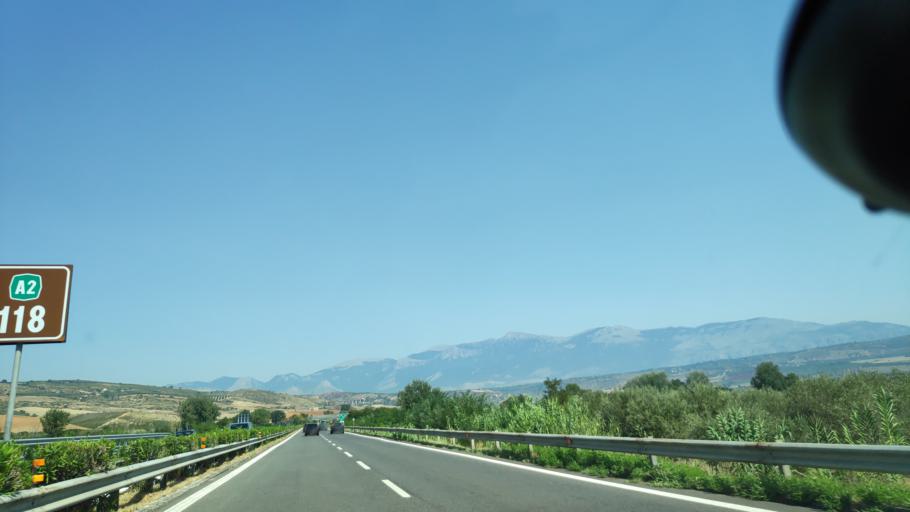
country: IT
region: Calabria
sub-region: Provincia di Cosenza
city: Firmo
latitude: 39.7288
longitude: 16.2355
